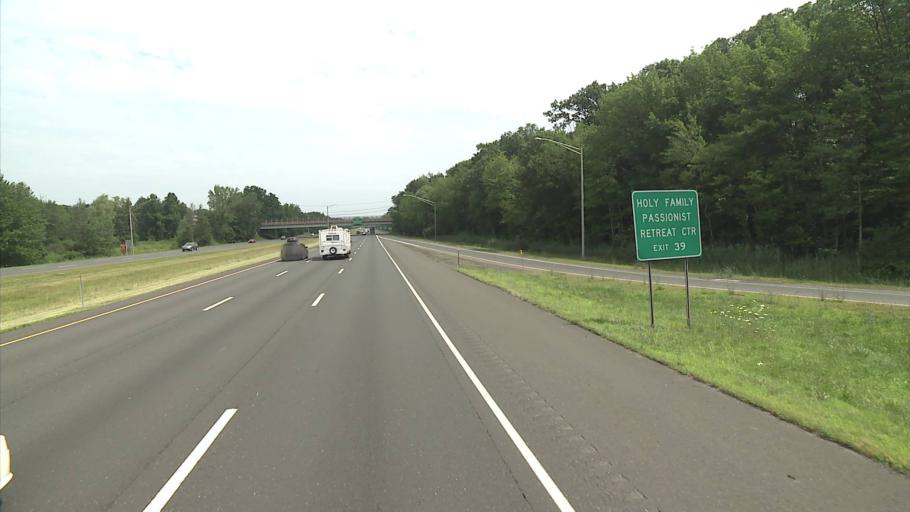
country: US
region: Connecticut
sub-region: Hartford County
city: Farmington
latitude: 41.7050
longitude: -72.8030
